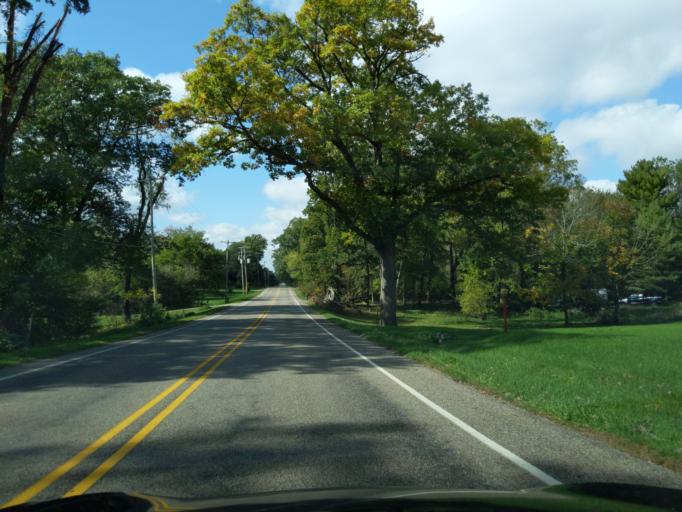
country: US
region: Michigan
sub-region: Eaton County
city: Charlotte
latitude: 42.5676
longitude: -84.7775
